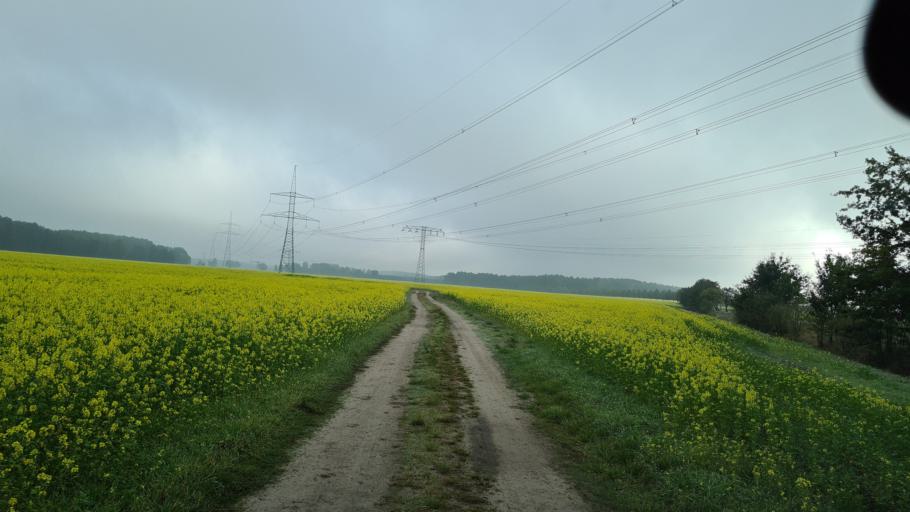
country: DE
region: Brandenburg
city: Schonewalde
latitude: 51.6555
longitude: 13.6070
